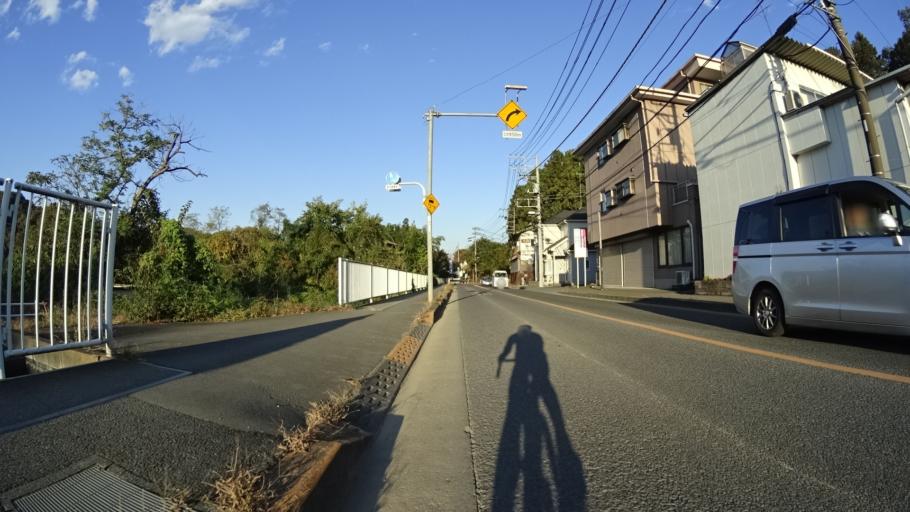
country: JP
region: Tokyo
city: Hachioji
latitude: 35.6816
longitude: 139.2748
